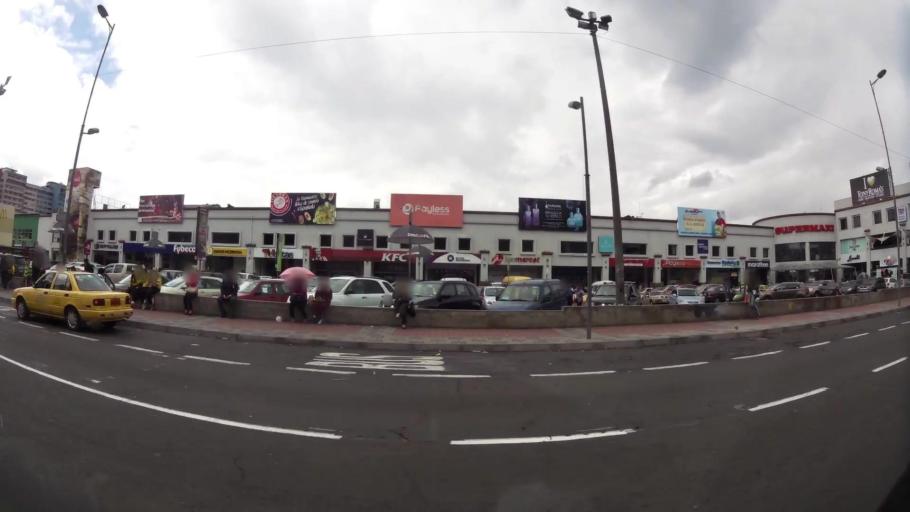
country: EC
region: Pichincha
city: Quito
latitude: -0.1773
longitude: -78.4857
